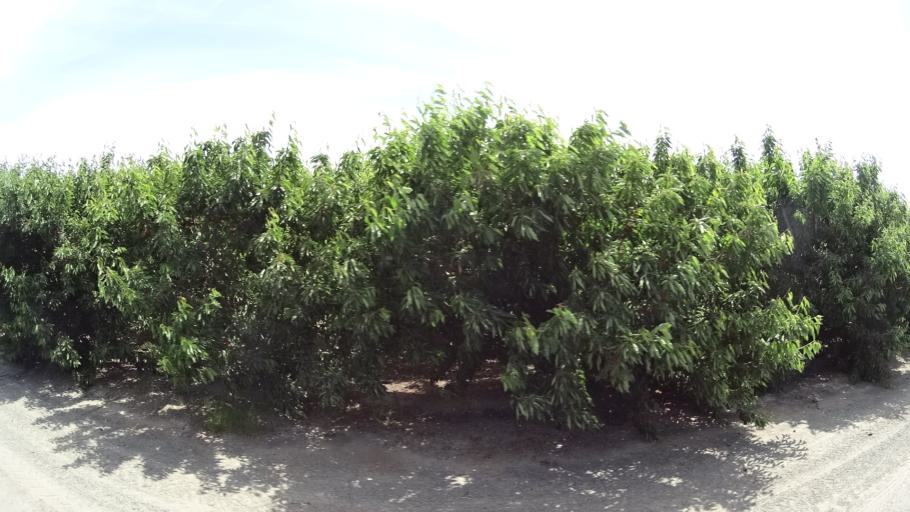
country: US
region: California
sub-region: Kings County
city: Lucerne
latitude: 36.3710
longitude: -119.6910
